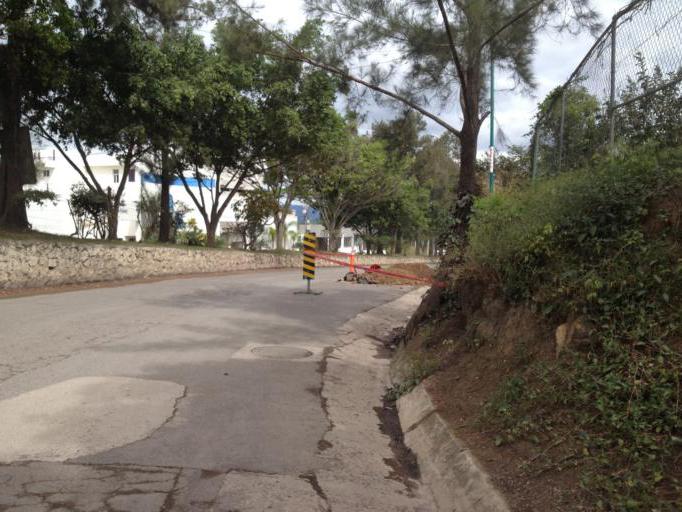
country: MX
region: Veracruz
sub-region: Emiliano Zapata
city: Las Trancas
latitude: 19.5084
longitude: -96.8586
